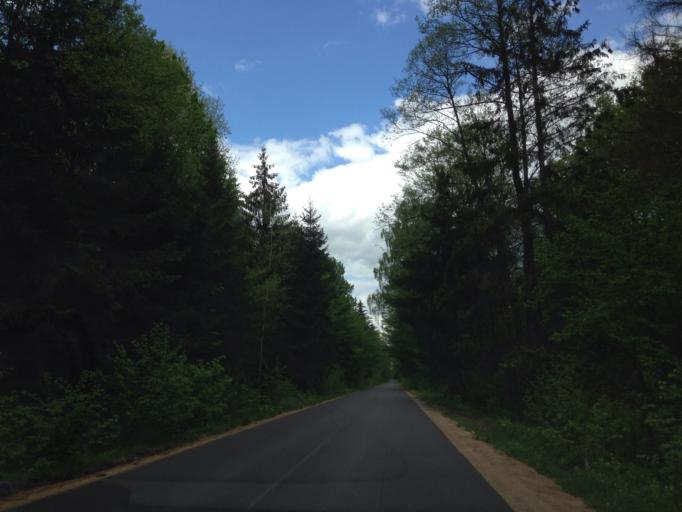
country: PL
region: Podlasie
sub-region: Powiat grajewski
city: Radzilow
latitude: 53.3370
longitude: 22.5988
